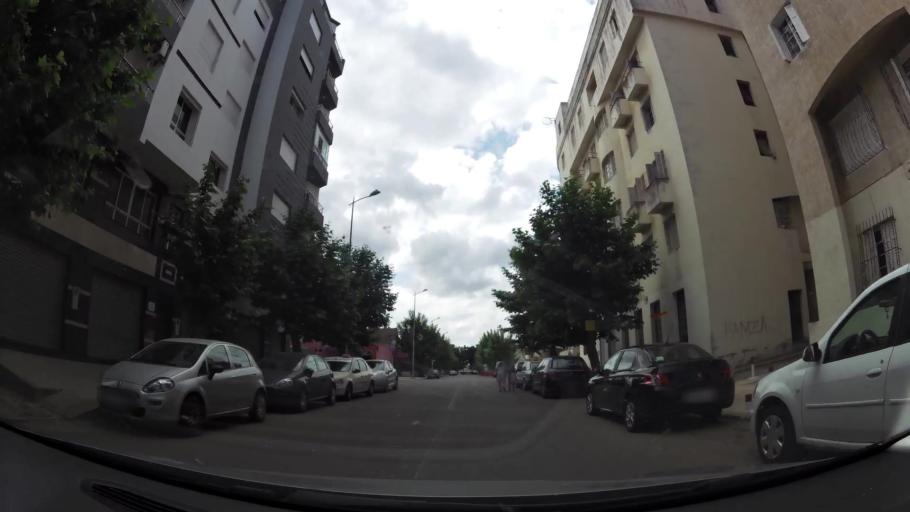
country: MA
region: Gharb-Chrarda-Beni Hssen
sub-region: Kenitra Province
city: Kenitra
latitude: 34.2546
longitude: -6.5862
